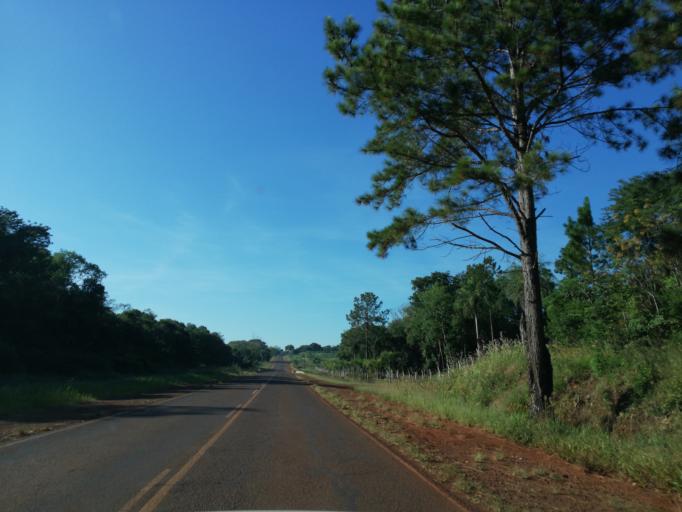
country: AR
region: Misiones
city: Gobernador Roca
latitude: -27.1829
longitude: -55.4515
